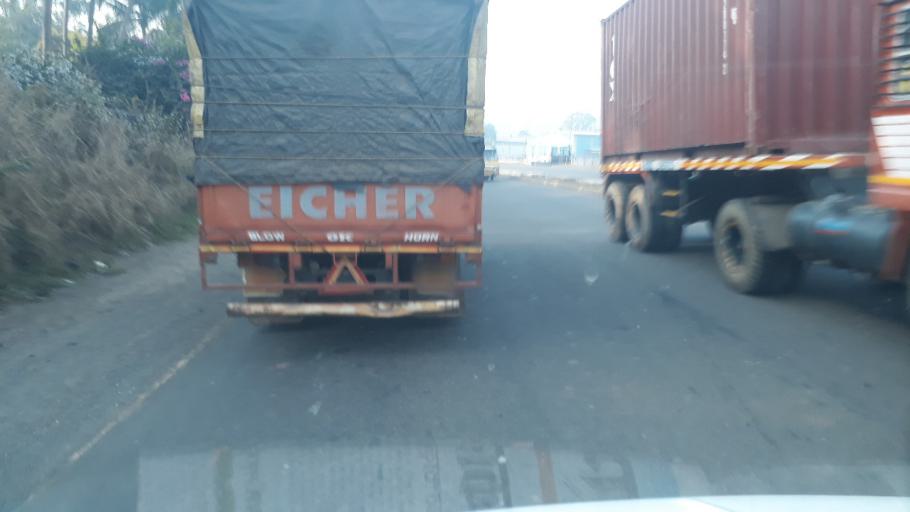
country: IN
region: Maharashtra
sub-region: Raigarh
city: Kalundri
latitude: 18.9185
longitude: 73.1240
